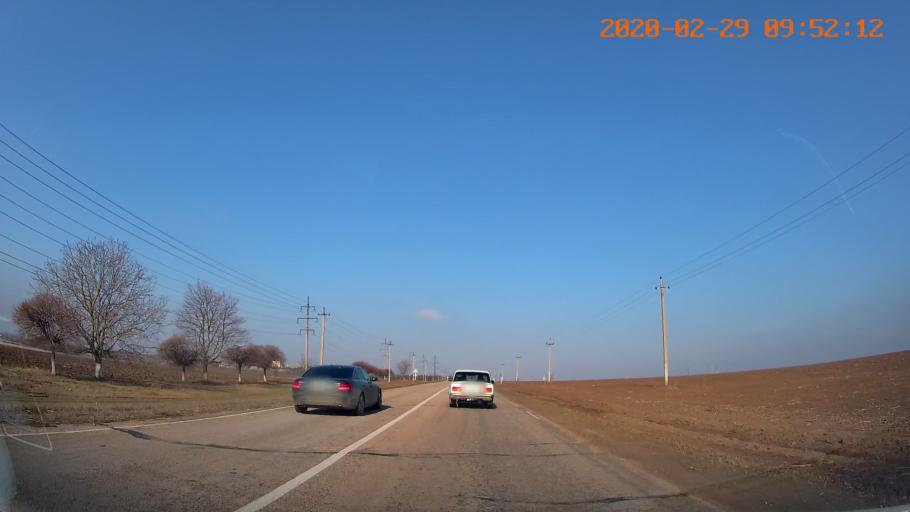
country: MD
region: Telenesti
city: Slobozia
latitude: 46.7145
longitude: 29.7330
